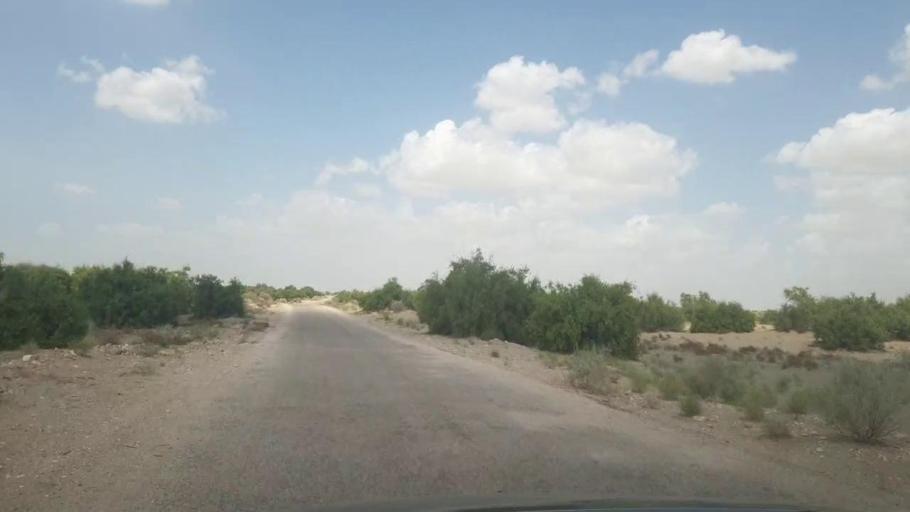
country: PK
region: Sindh
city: Kot Diji
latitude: 27.2284
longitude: 69.1150
